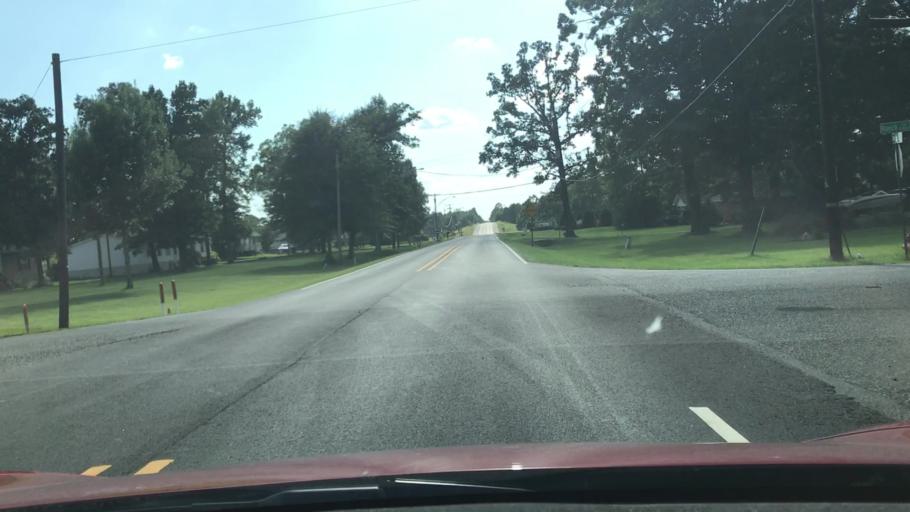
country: US
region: Louisiana
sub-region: Bossier Parish
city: Bossier City
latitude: 32.3909
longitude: -93.7450
